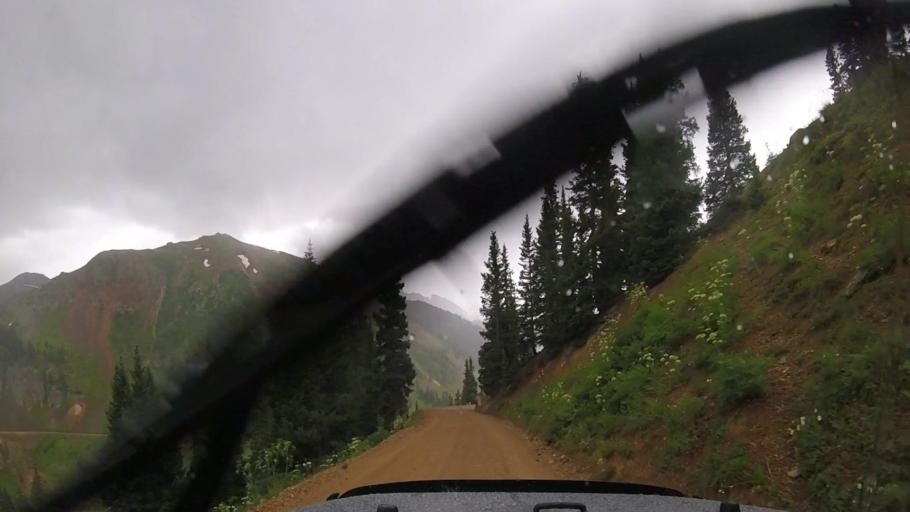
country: US
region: Colorado
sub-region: San Juan County
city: Silverton
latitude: 37.9100
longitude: -107.6452
